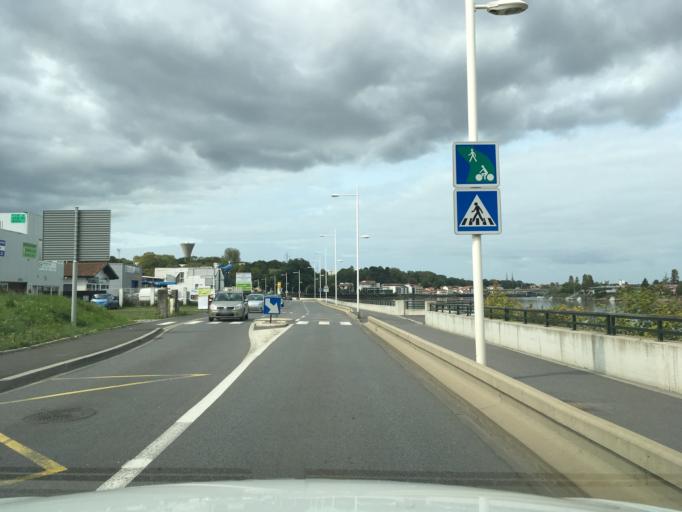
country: FR
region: Aquitaine
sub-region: Departement des Pyrenees-Atlantiques
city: Mouguerre
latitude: 43.4843
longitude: -1.4481
